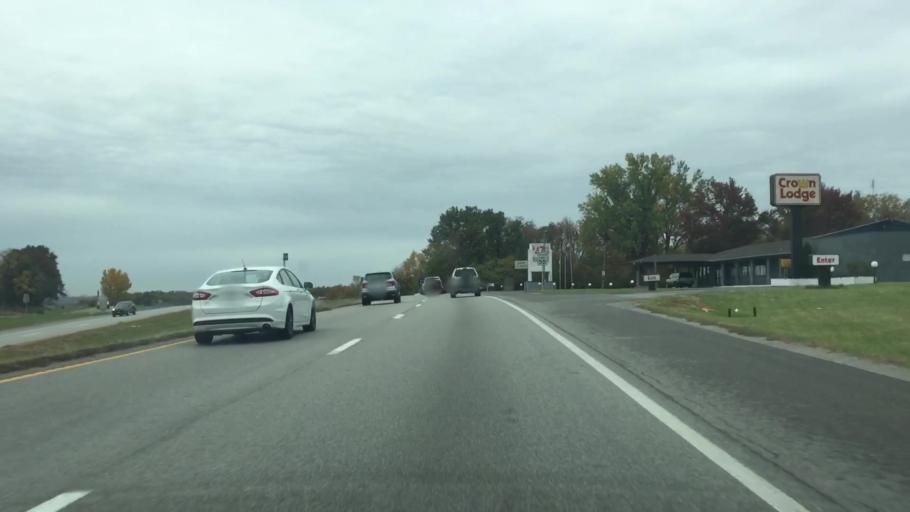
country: US
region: Missouri
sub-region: Jackson County
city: Raytown
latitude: 39.0049
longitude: -94.4851
